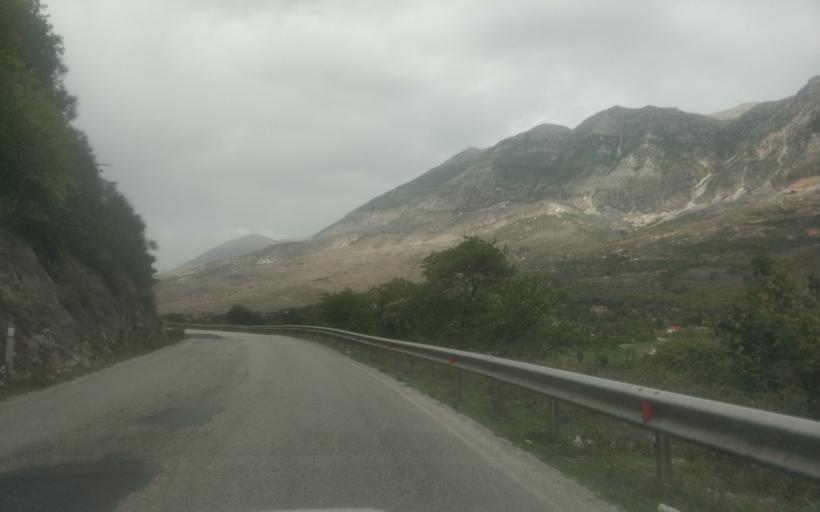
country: AL
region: Gjirokaster
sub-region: Rrethi i Gjirokastres
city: Picar
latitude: 40.2279
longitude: 20.0851
